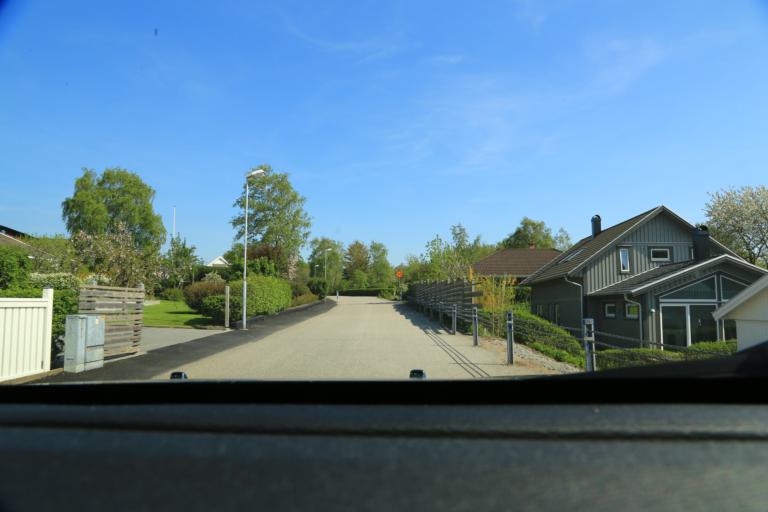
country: SE
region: Halland
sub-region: Varbergs Kommun
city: Varberg
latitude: 57.1368
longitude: 12.2867
